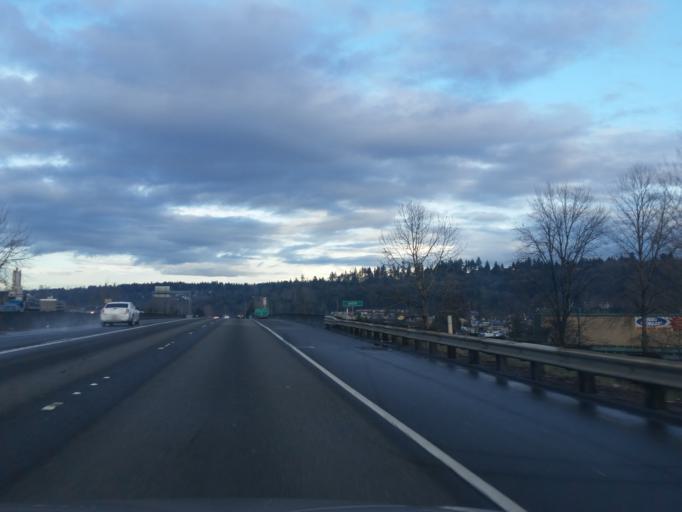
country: US
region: Washington
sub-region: King County
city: Kent
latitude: 47.3943
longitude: -122.2341
